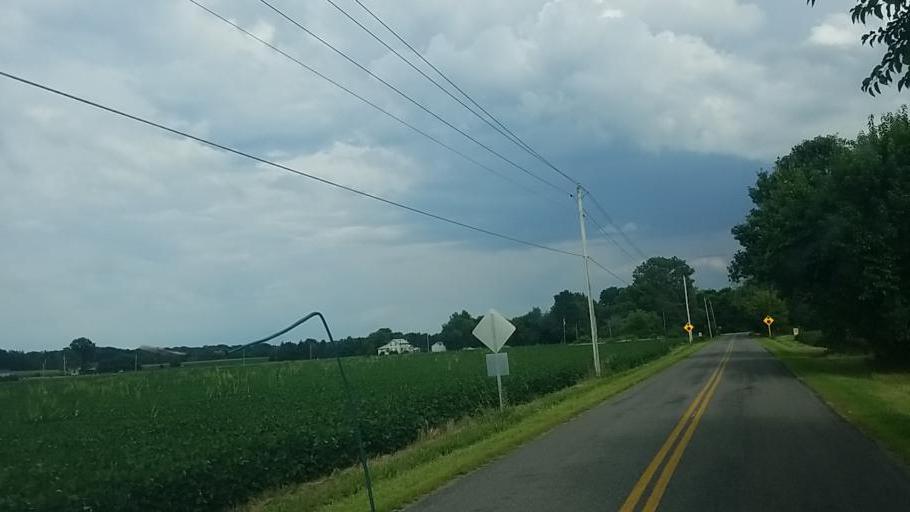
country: US
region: Ohio
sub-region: Wayne County
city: Creston
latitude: 40.9956
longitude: -81.8925
